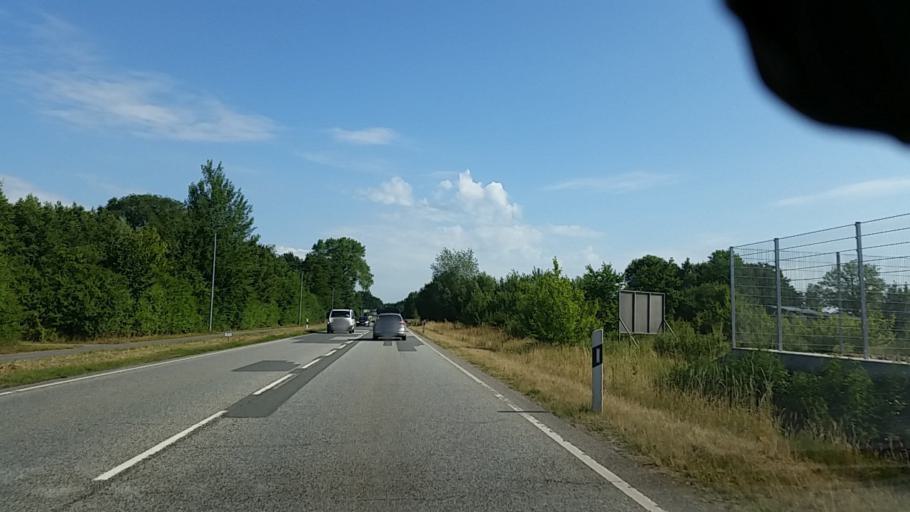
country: DE
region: Schleswig-Holstein
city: Oersdorf
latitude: 53.8202
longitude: 9.9713
